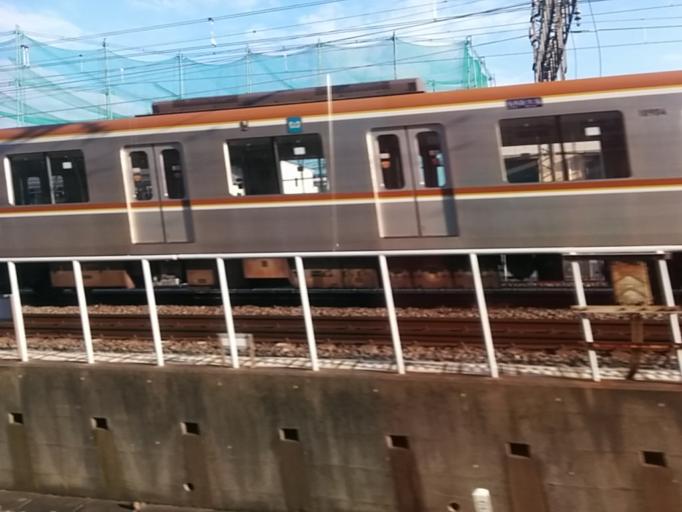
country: JP
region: Saitama
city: Wako
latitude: 35.7896
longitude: 139.6098
